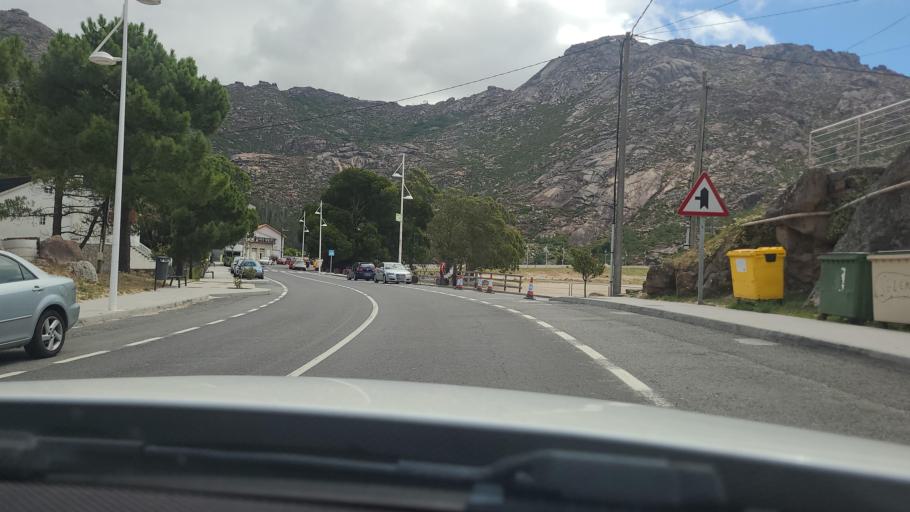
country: ES
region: Galicia
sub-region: Provincia da Coruna
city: Corcubion
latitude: 42.9086
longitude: -9.1285
